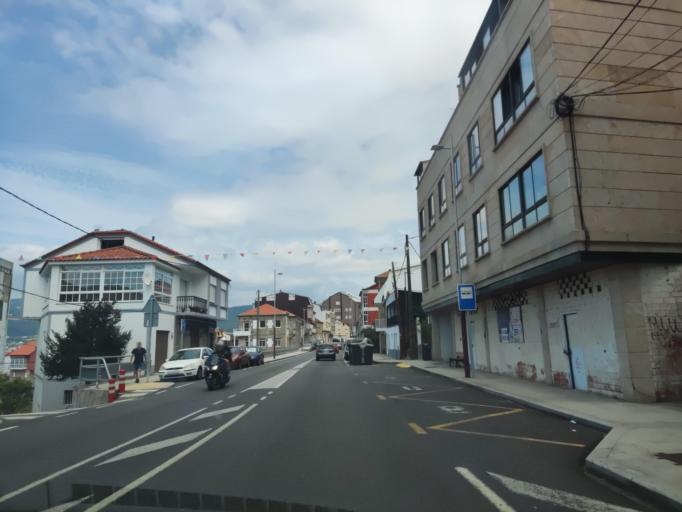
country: ES
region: Galicia
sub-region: Provincia de Pontevedra
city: Vigo
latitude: 42.2640
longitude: -8.6741
